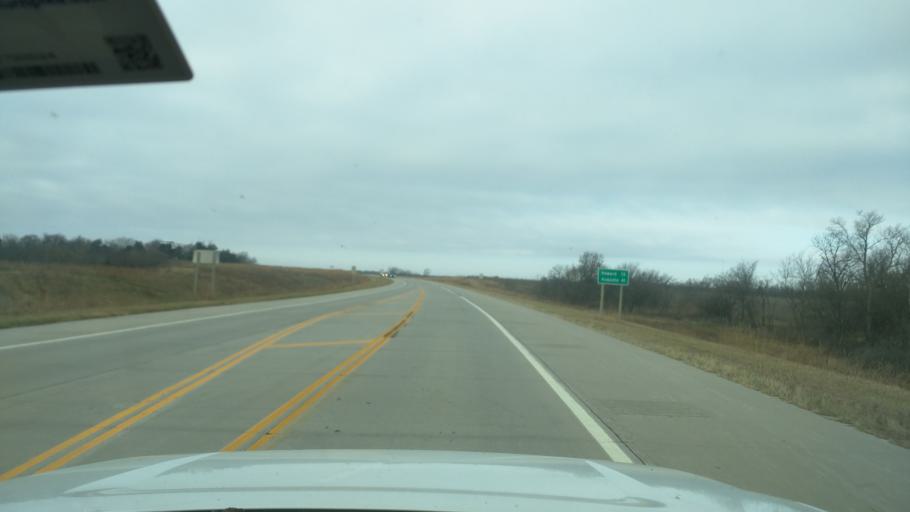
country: US
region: Kansas
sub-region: Elk County
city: Howard
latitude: 37.6370
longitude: -96.2363
